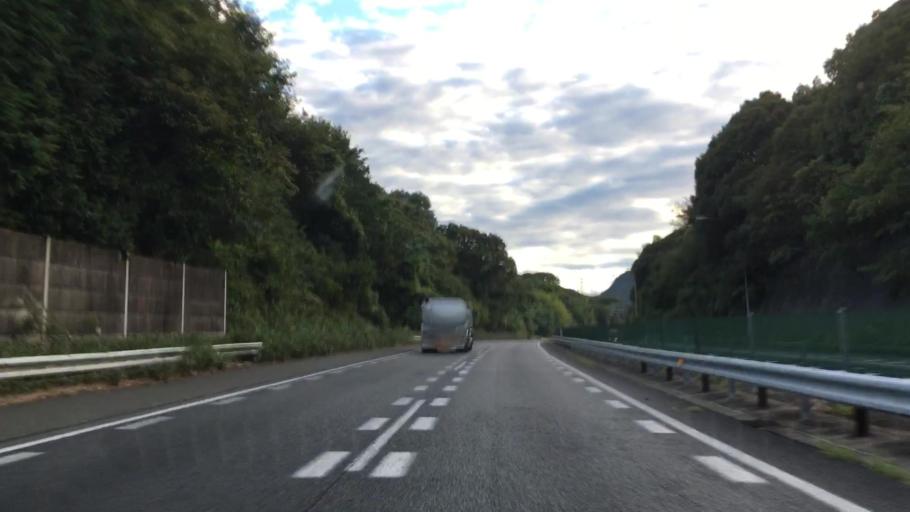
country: JP
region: Yamaguchi
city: Shimonoseki
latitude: 34.0480
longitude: 131.0017
